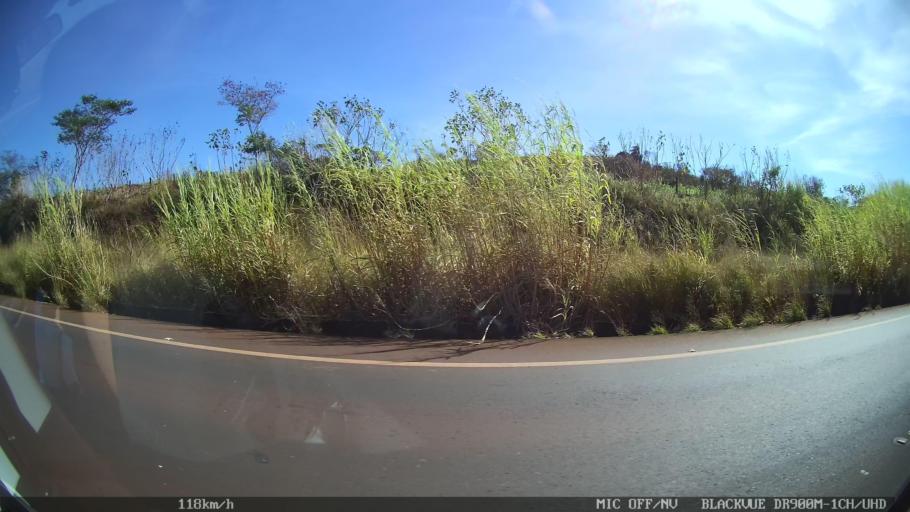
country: BR
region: Sao Paulo
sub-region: Sao Joaquim Da Barra
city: Sao Joaquim da Barra
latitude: -20.5573
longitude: -47.6818
